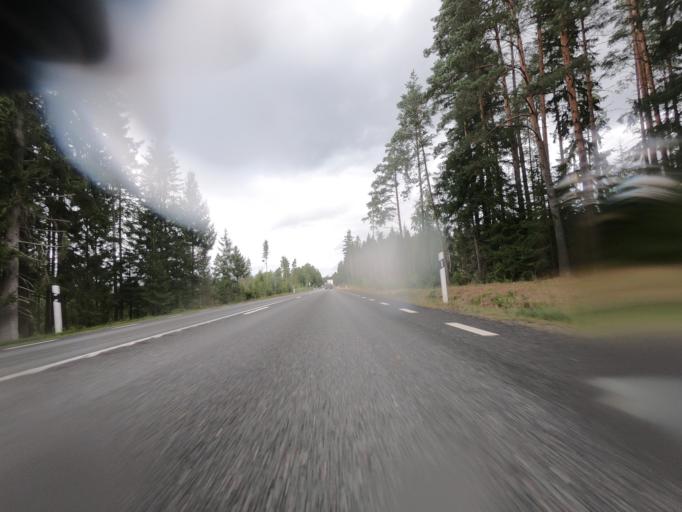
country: SE
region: Joenkoeping
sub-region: Savsjo Kommun
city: Vrigstad
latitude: 57.4315
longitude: 14.3205
